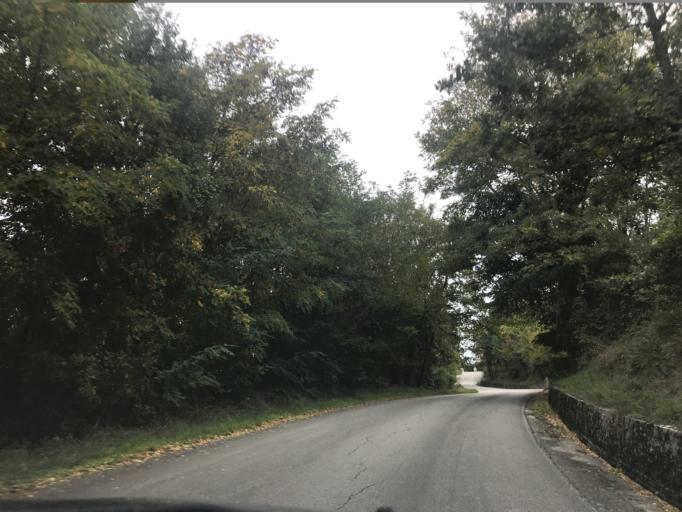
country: IT
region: Molise
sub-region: Provincia di Campobasso
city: Duronia
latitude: 41.6616
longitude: 14.4612
